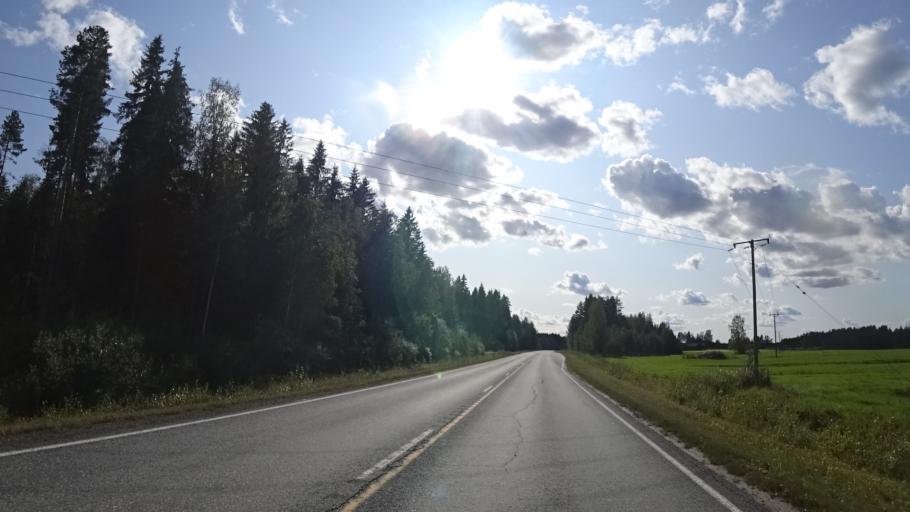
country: FI
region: North Karelia
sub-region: Keski-Karjala
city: Kitee
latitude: 62.0938
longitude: 30.0561
